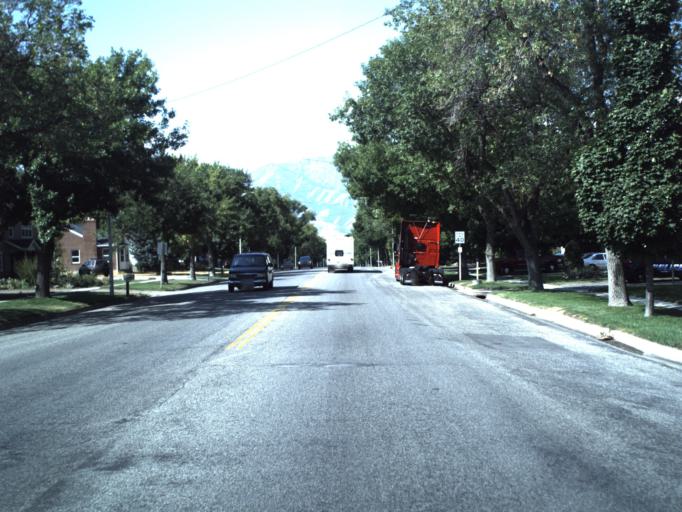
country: US
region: Utah
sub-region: Cache County
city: Hyrum
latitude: 41.6338
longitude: -111.8412
